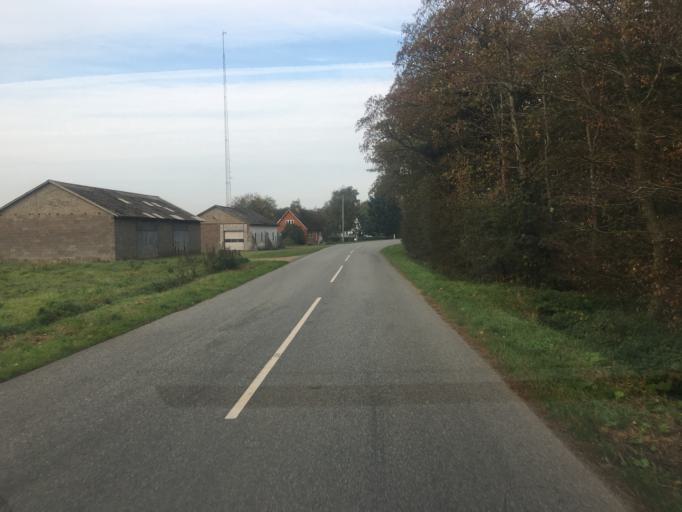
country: DK
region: South Denmark
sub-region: Tonder Kommune
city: Toftlund
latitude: 55.1152
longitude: 9.0766
